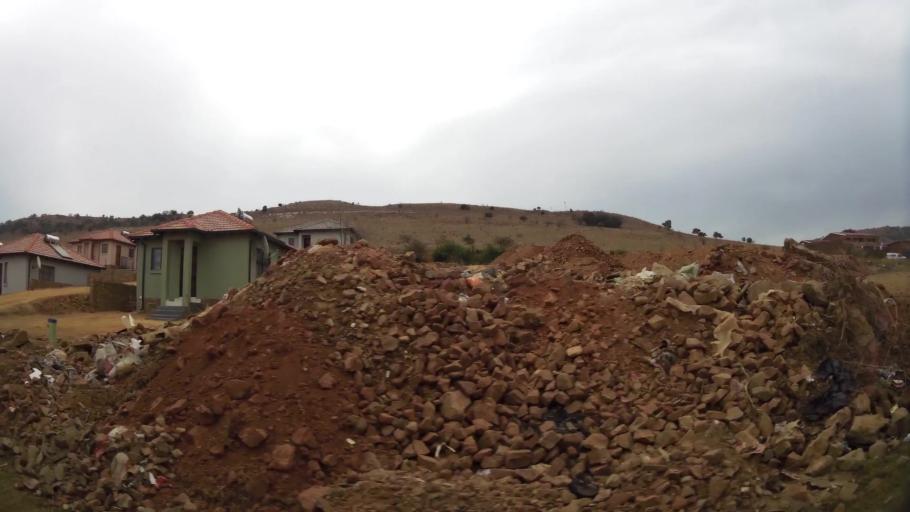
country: ZA
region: Gauteng
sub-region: City of Tshwane Metropolitan Municipality
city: Pretoria
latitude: -25.7016
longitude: 28.3386
